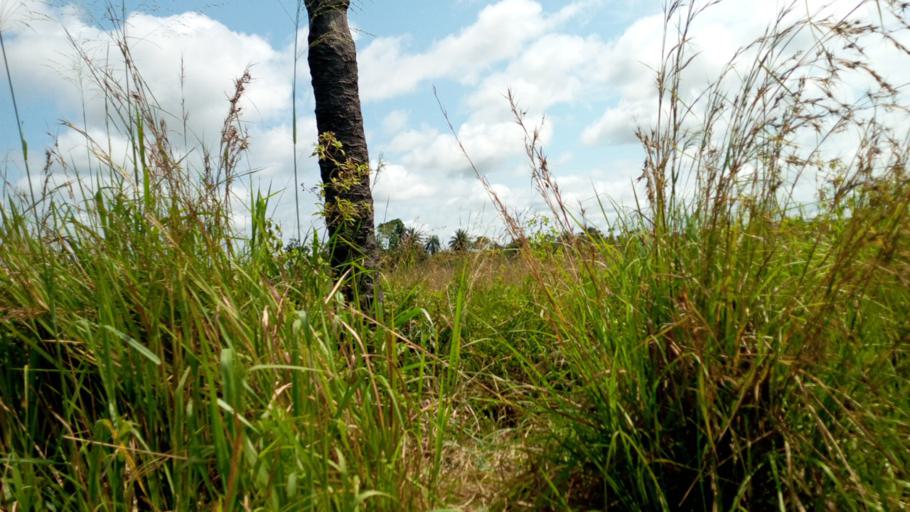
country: CD
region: Bandundu
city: Bandundu
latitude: -3.5010
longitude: 17.6344
